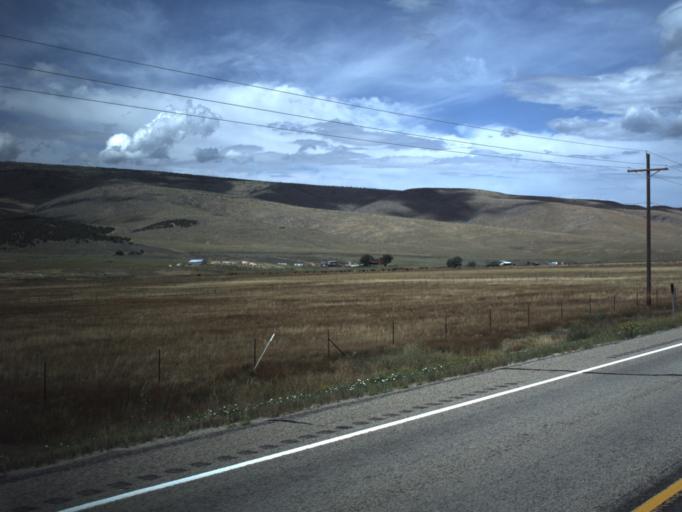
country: US
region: Utah
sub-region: Sanpete County
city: Fairview
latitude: 39.7963
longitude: -111.4992
